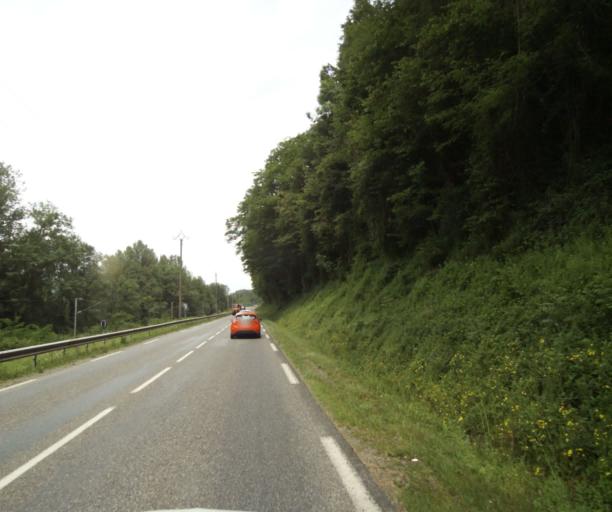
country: FR
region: Rhone-Alpes
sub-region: Departement de la Haute-Savoie
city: Perrignier
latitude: 46.3168
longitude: 6.4415
